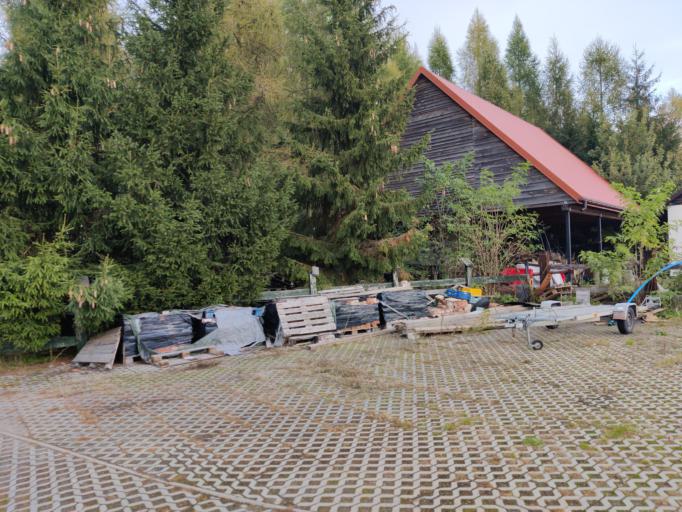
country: PL
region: Masovian Voivodeship
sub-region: Powiat plocki
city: Lack
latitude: 52.4210
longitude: 19.6317
